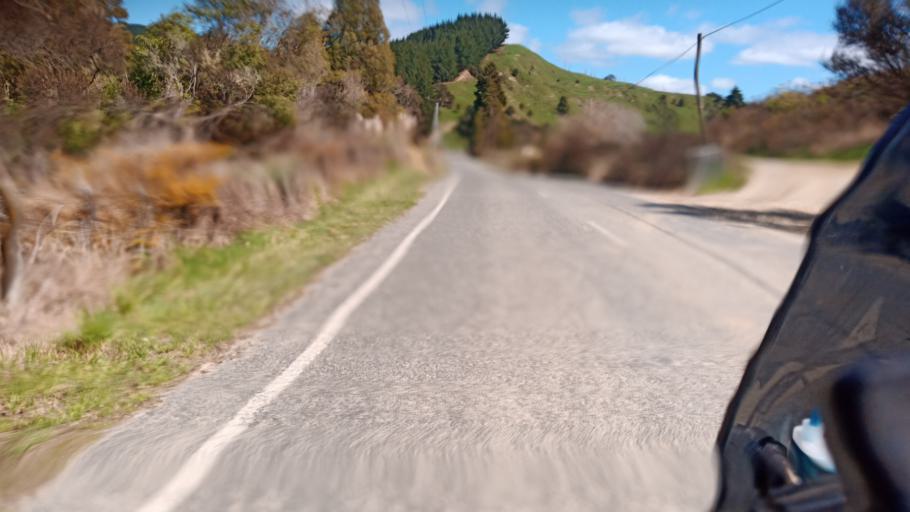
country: NZ
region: Gisborne
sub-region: Gisborne District
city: Gisborne
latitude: -38.7869
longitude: 177.7967
